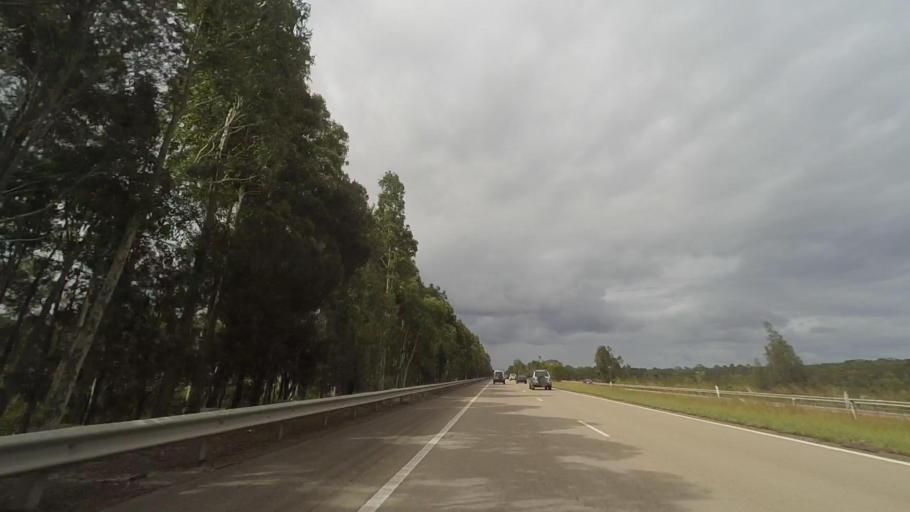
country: AU
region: New South Wales
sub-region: Port Stephens Shire
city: Raymond Terrace
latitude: -32.7305
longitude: 151.7832
